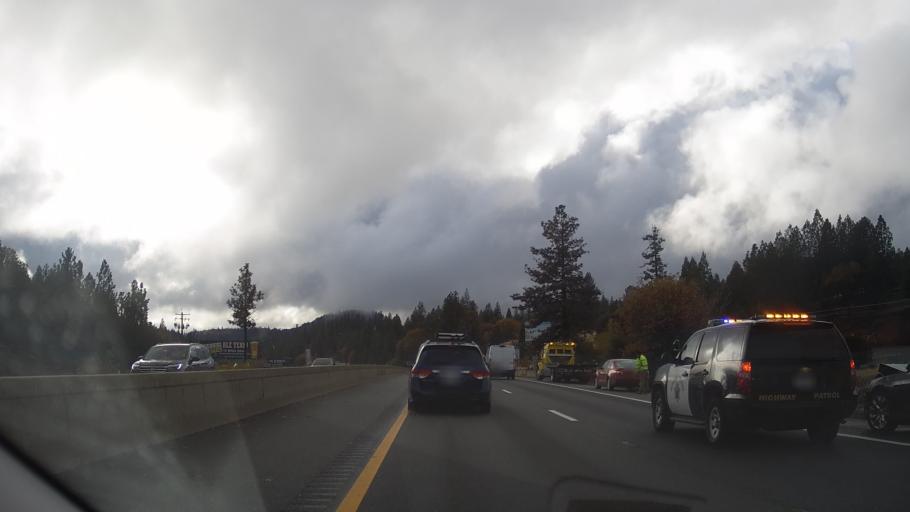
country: US
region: California
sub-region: Placer County
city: Colfax
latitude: 39.0894
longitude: -120.9532
